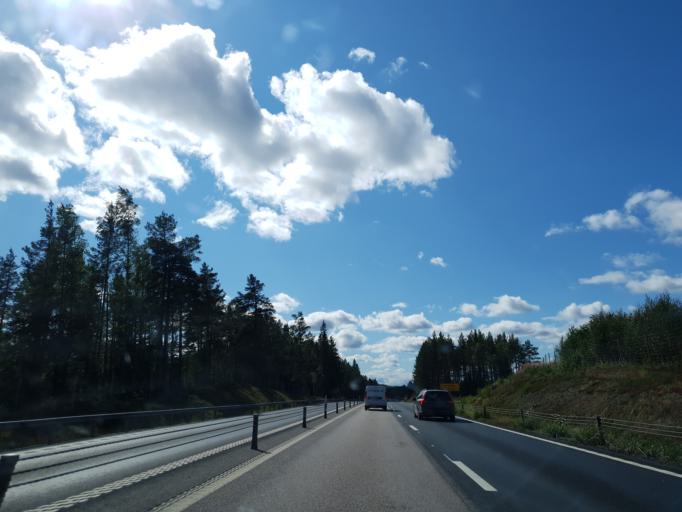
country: SE
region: Vaesterbotten
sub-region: Nordmalings Kommun
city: Nordmaling
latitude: 63.4876
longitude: 19.3089
